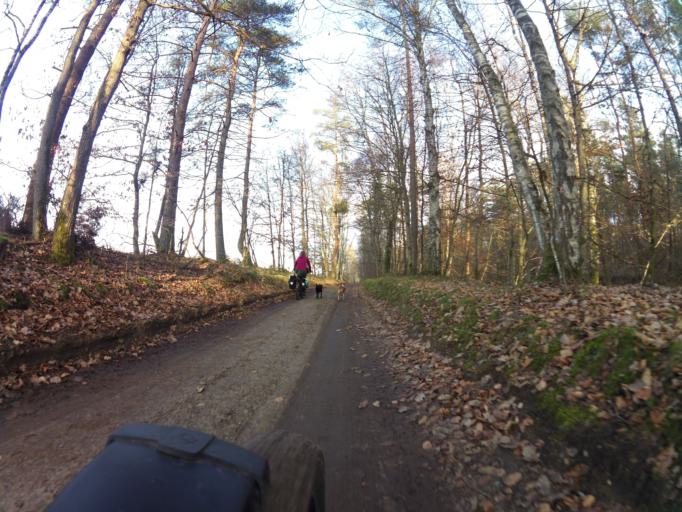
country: PL
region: West Pomeranian Voivodeship
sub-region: Powiat koszalinski
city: Polanow
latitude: 54.1089
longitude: 16.6514
